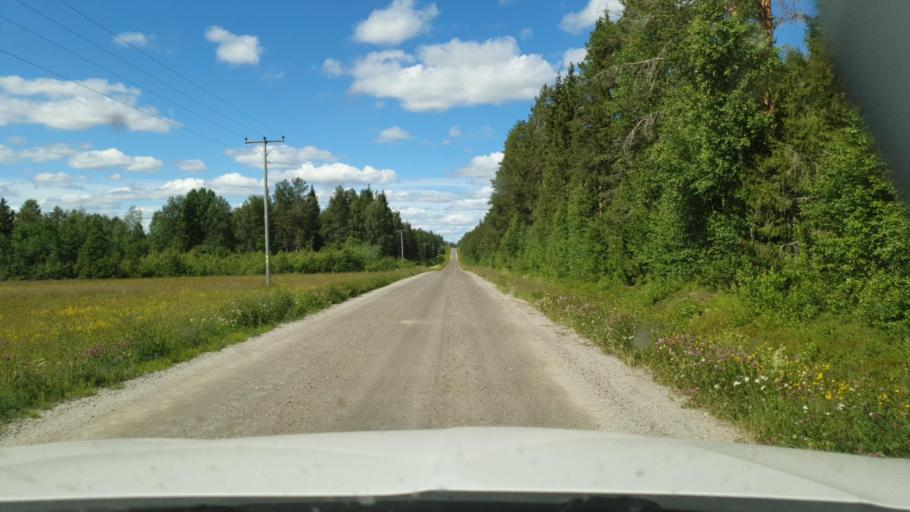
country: SE
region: Vaesterbotten
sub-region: Skelleftea Kommun
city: Backa
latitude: 65.1706
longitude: 21.1111
